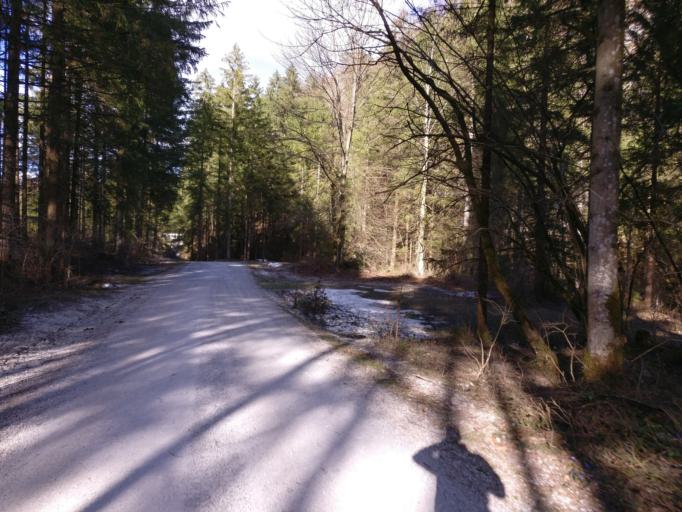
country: AT
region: Salzburg
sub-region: Politischer Bezirk Hallein
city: Golling an der Salzach
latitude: 47.5813
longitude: 13.1486
